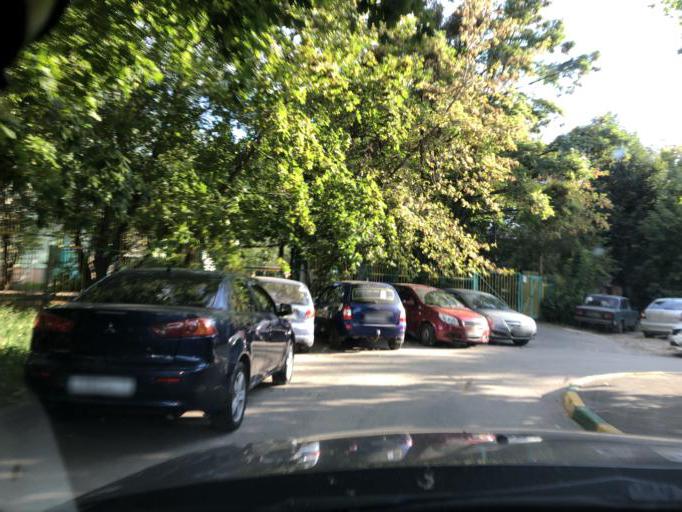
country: RU
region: Tula
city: Tula
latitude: 54.2105
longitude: 37.6060
